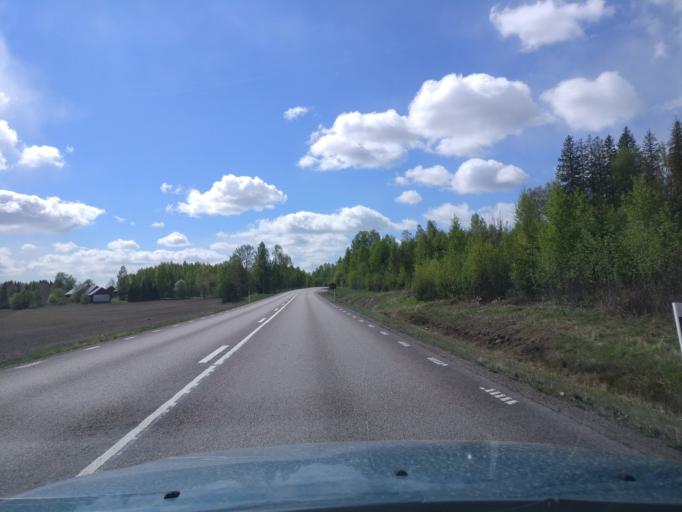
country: SE
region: Vaermland
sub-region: Karlstads Kommun
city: Molkom
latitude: 59.5508
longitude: 13.6567
